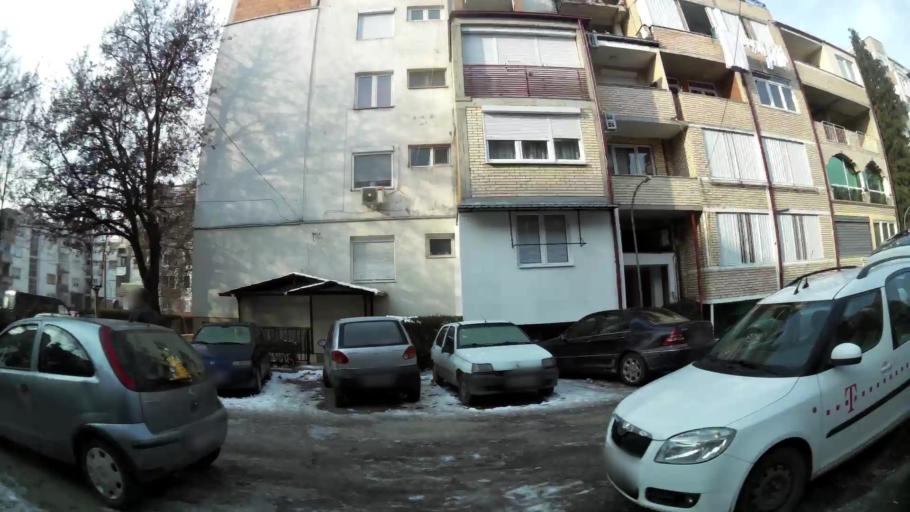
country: MK
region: Cair
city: Cair
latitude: 42.0216
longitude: 21.4321
